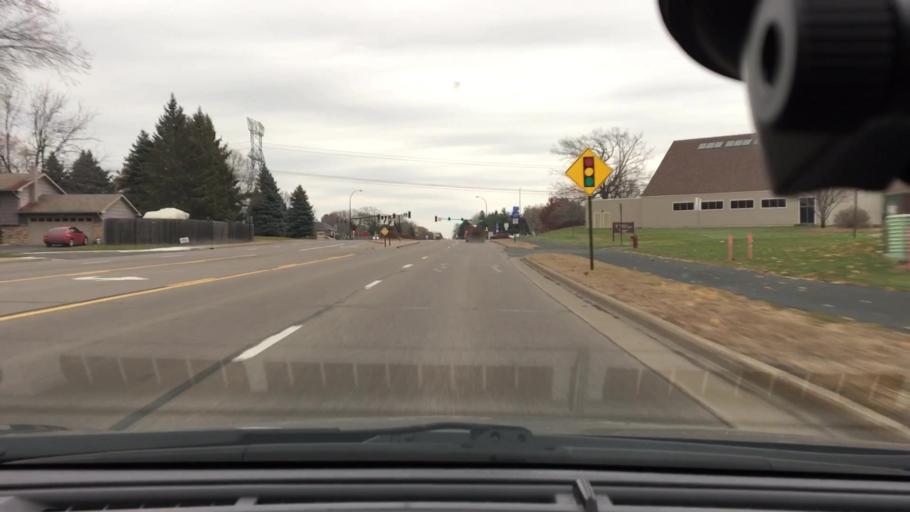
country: US
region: Minnesota
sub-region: Hennepin County
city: Osseo
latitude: 45.1235
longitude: -93.4507
